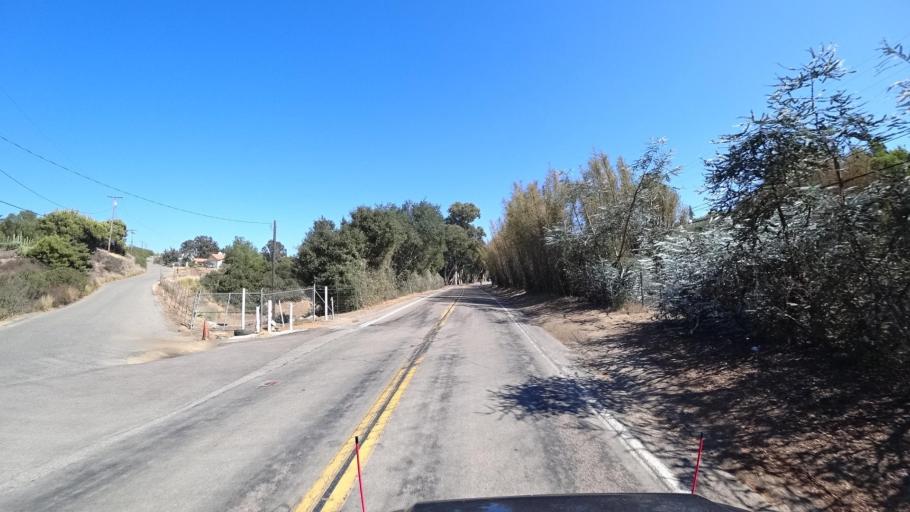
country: US
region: California
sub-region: San Diego County
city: Hidden Meadows
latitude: 33.2821
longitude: -117.1154
